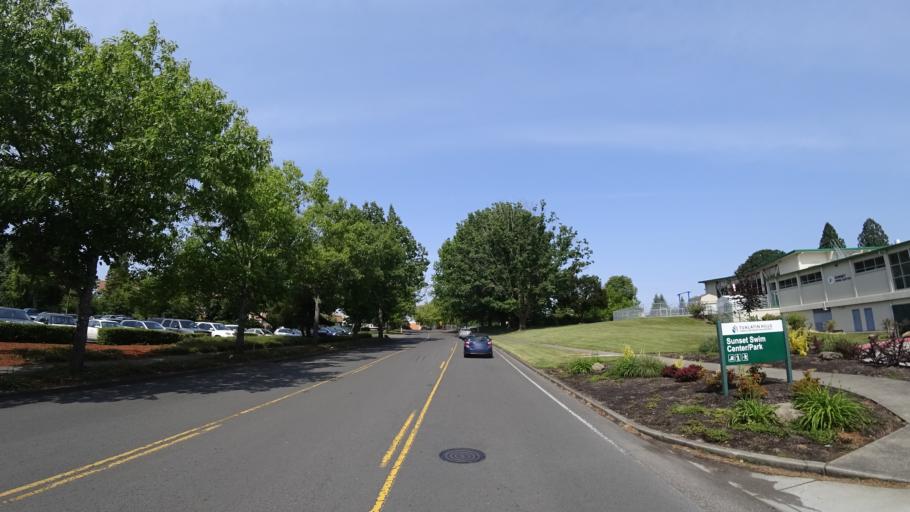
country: US
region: Oregon
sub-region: Washington County
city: Cedar Mill
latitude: 45.5256
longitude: -122.8182
